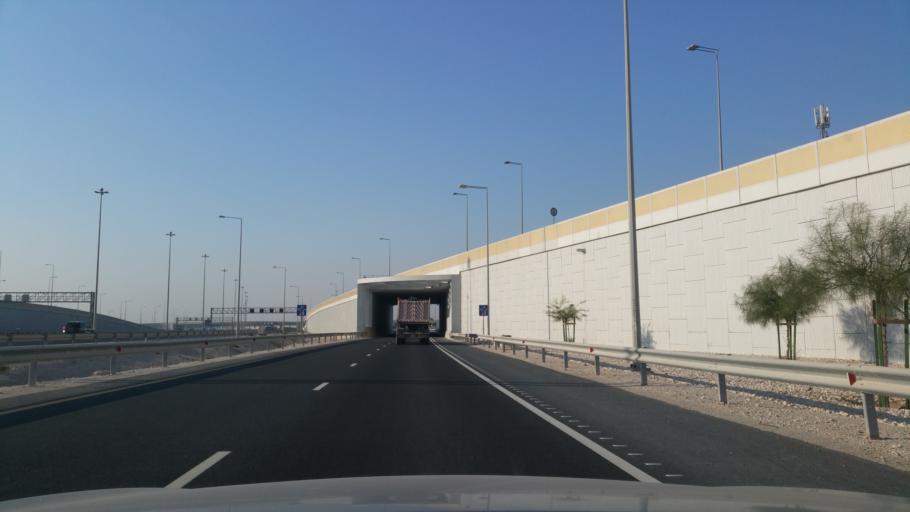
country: QA
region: Al Wakrah
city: Al Wakrah
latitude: 25.1547
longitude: 51.5736
